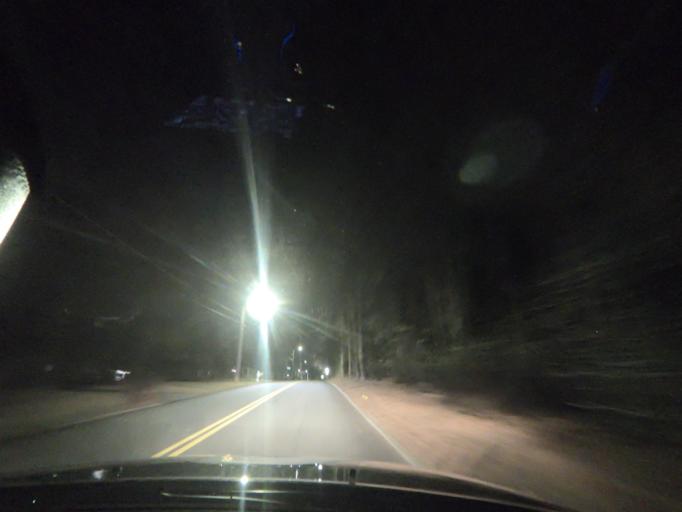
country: US
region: Georgia
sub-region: Fulton County
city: College Park
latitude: 33.6607
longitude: -84.4698
